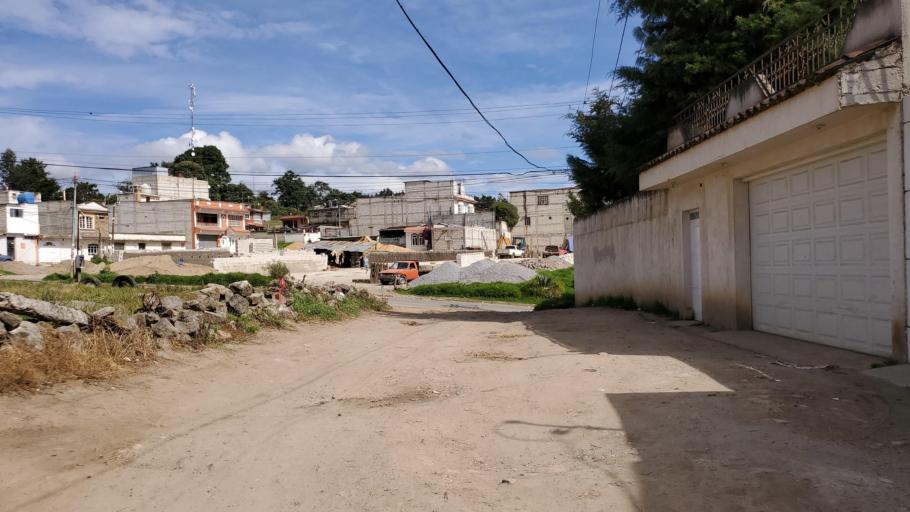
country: GT
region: Quetzaltenango
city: Quetzaltenango
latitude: 14.8385
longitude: -91.5406
